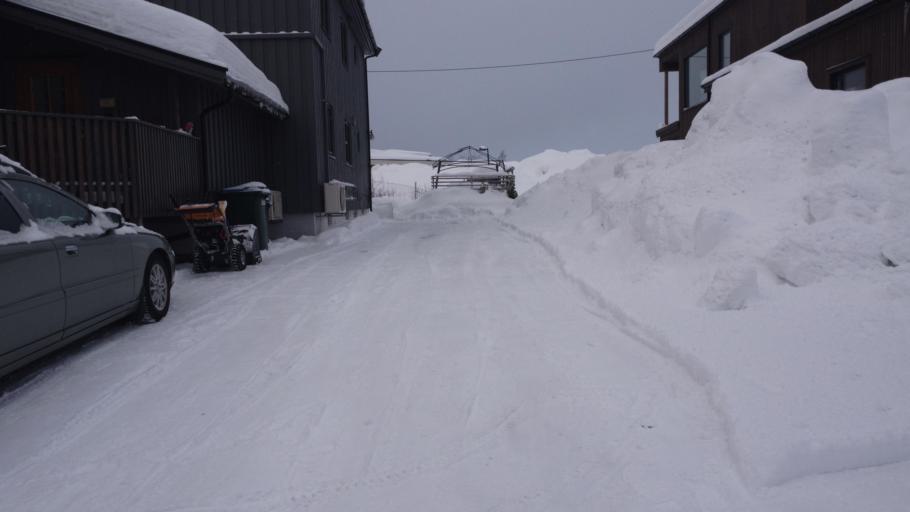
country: NO
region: Nordland
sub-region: Rana
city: Mo i Rana
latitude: 66.3147
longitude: 14.1507
